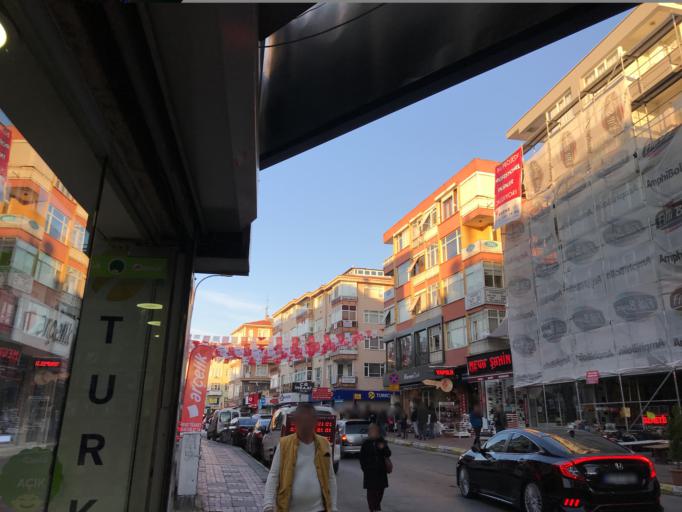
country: TR
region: Istanbul
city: Maltepe
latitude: 40.9259
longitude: 29.1322
